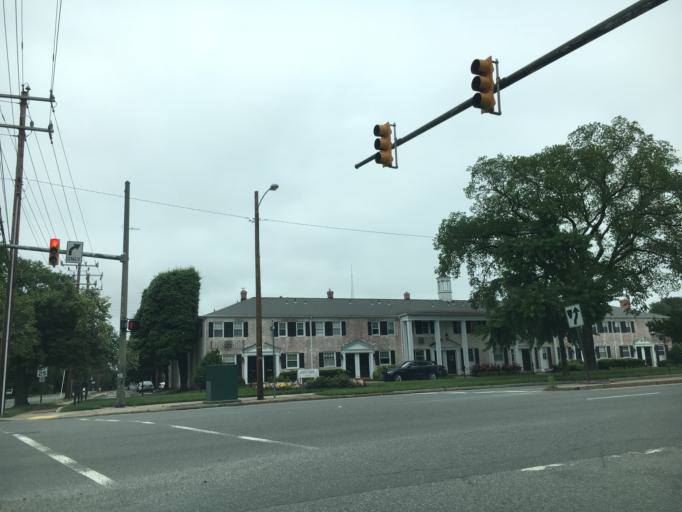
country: US
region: Virginia
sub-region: City of Richmond
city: Richmond
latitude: 37.5605
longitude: -77.4896
